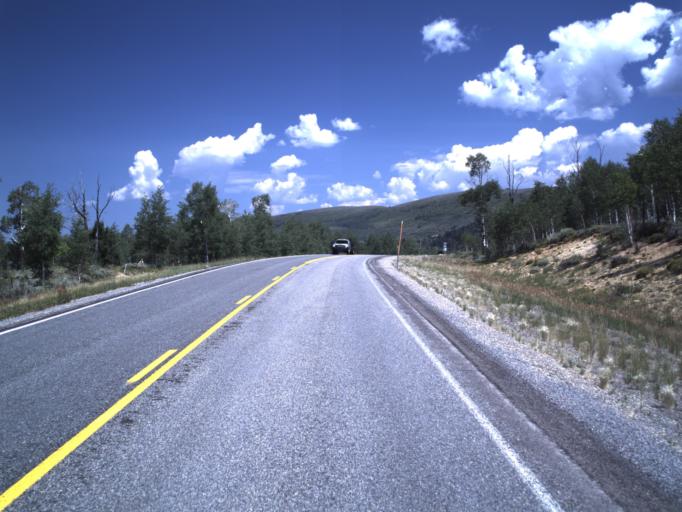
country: US
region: Utah
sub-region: Carbon County
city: Helper
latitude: 39.8521
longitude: -111.1274
